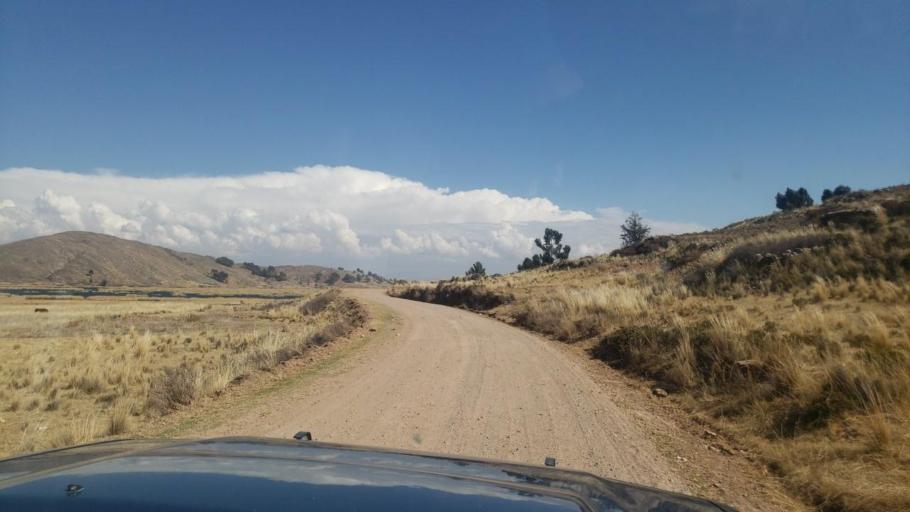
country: BO
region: La Paz
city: Huatajata
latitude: -16.3374
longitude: -68.6824
